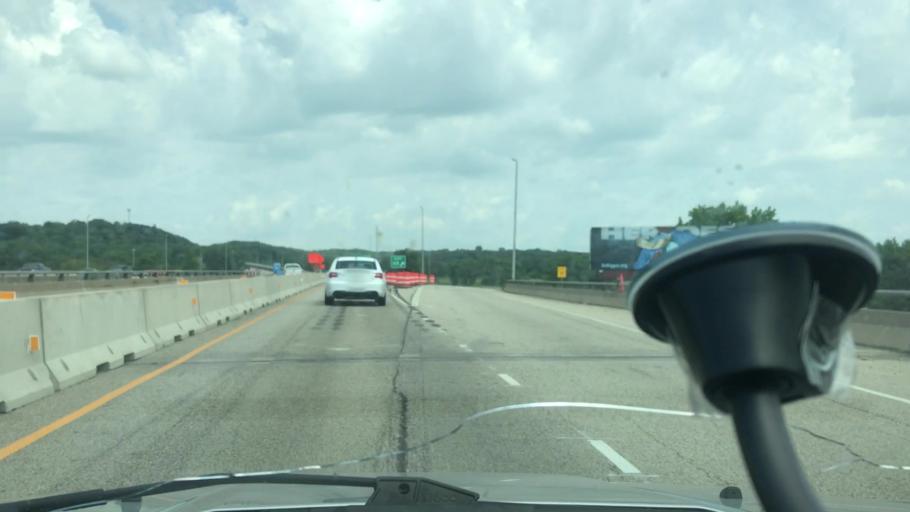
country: US
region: Illinois
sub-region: Peoria County
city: Bartonville
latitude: 40.6548
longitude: -89.6414
